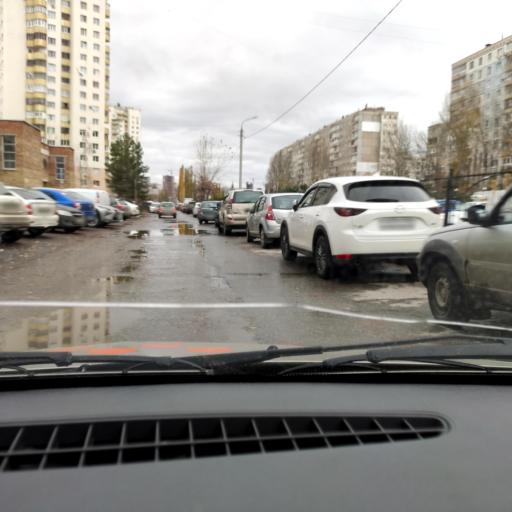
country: RU
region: Bashkortostan
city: Ufa
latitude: 54.7695
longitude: 56.0685
